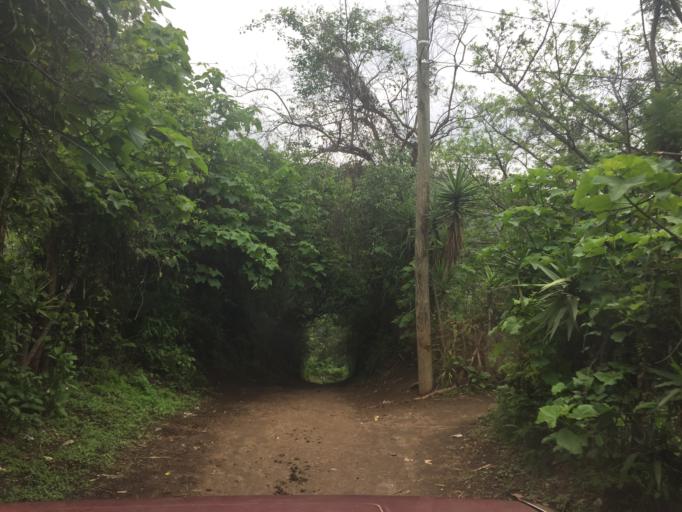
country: GT
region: Sacatepequez
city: Magdalena Milpas Altas
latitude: 14.5106
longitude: -90.6518
